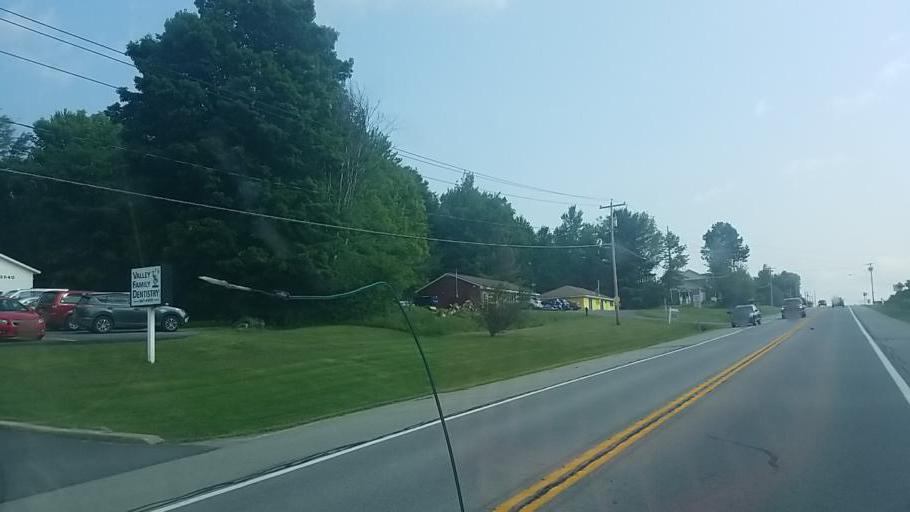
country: US
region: New York
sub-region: Fulton County
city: Broadalbin
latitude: 43.1053
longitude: -74.2719
